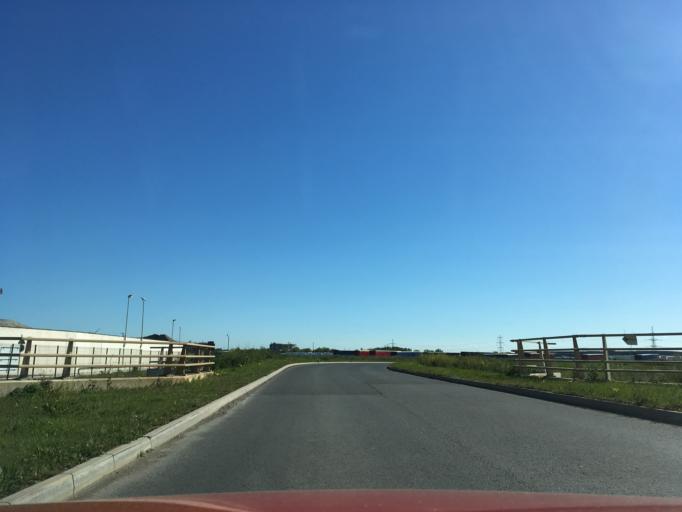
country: GB
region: England
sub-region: South Gloucestershire
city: Severn Beach
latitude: 51.5402
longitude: -2.6658
